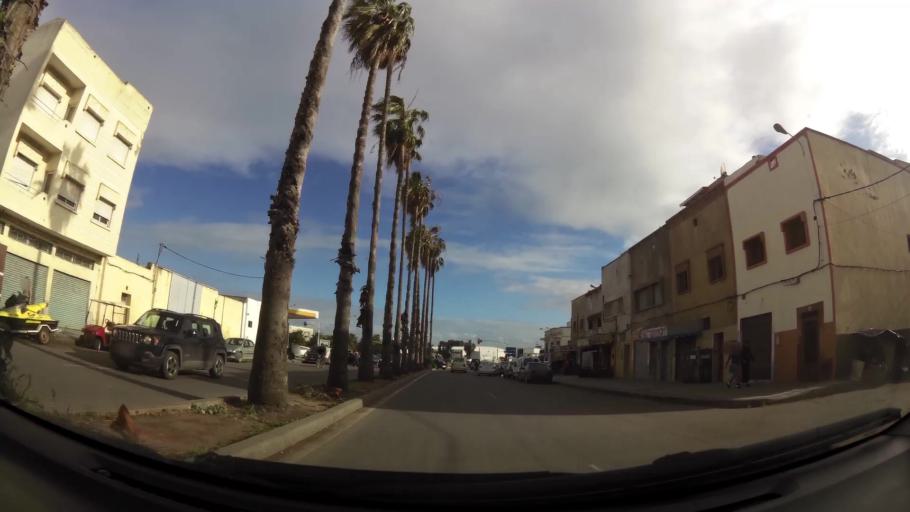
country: MA
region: Doukkala-Abda
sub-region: El-Jadida
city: El Jadida
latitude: 33.2492
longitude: -8.5177
